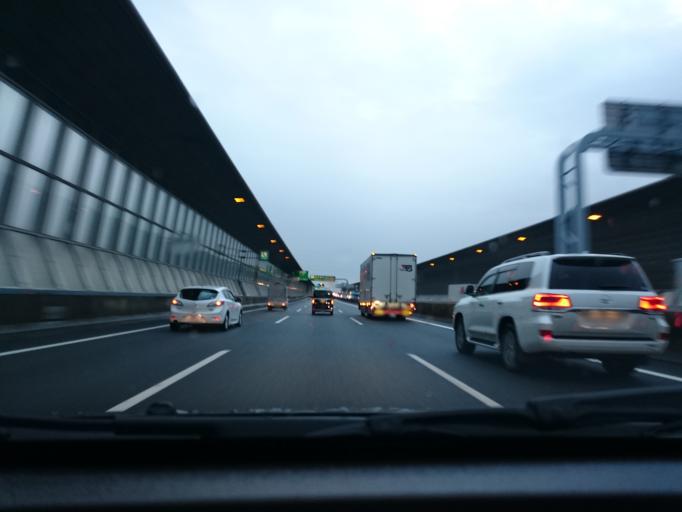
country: JP
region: Aichi
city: Obu
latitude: 35.0478
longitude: 136.9151
